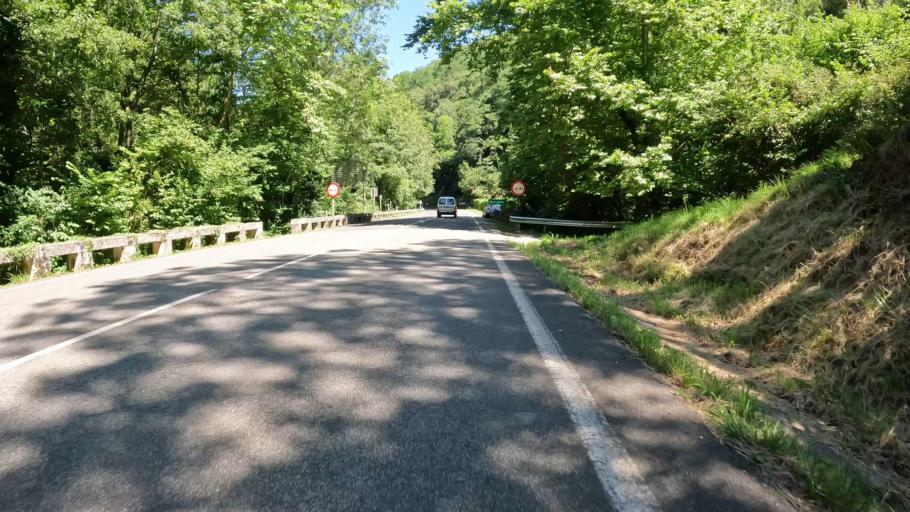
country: ES
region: Basque Country
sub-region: Provincia de Guipuzcoa
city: Oreja
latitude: 43.0727
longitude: -2.0116
